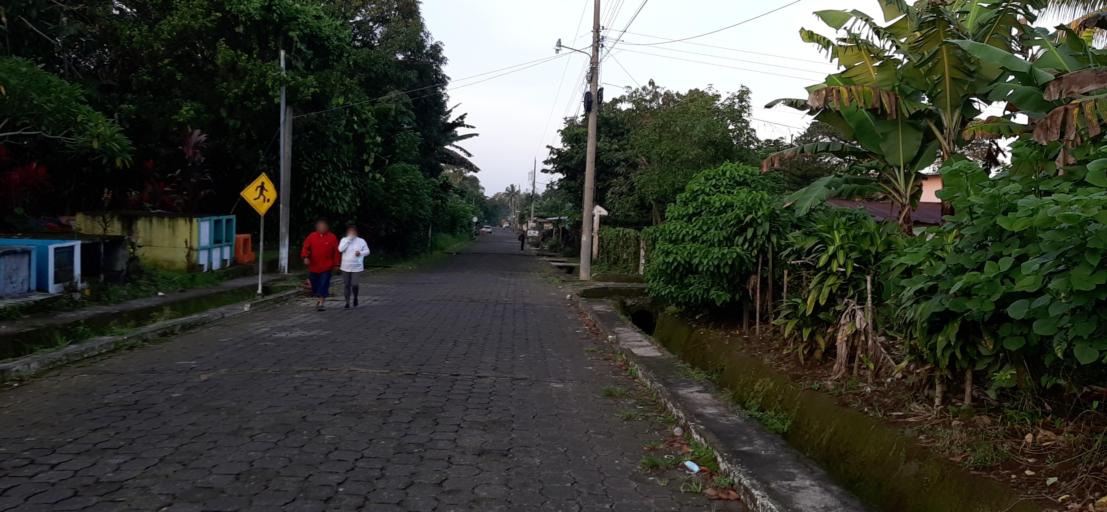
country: GT
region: Retalhuleu
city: San Felipe
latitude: 14.6221
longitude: -91.6034
